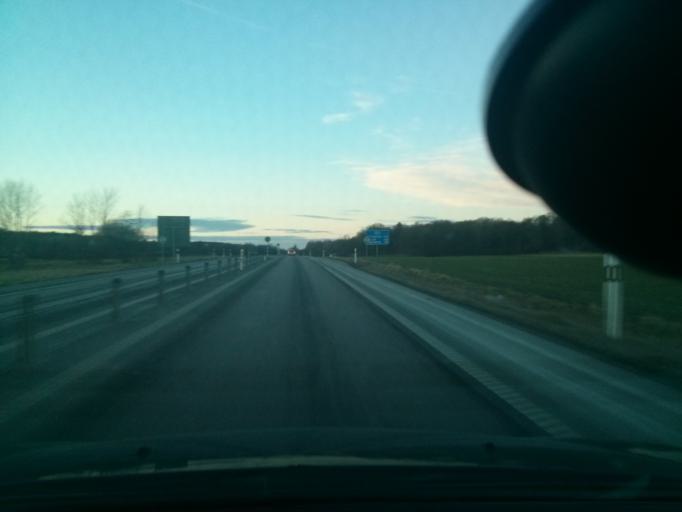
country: SE
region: Blekinge
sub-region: Ronneby Kommun
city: Kallinge
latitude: 56.2357
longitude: 15.2577
